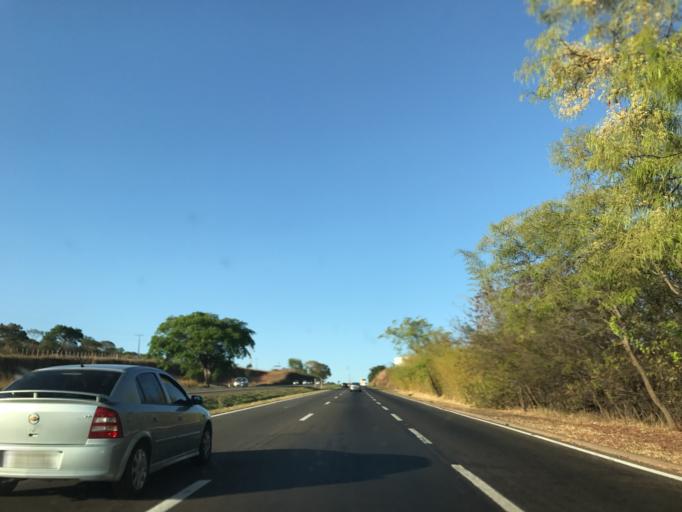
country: BR
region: Goias
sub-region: Goianapolis
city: Goianapolis
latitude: -16.4960
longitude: -49.1046
